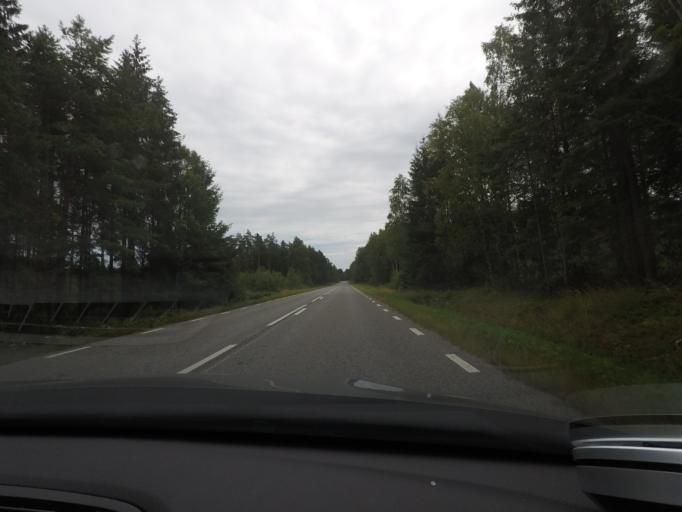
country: SE
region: Blekinge
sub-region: Olofstroms Kommun
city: Olofstroem
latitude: 56.4648
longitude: 14.6303
